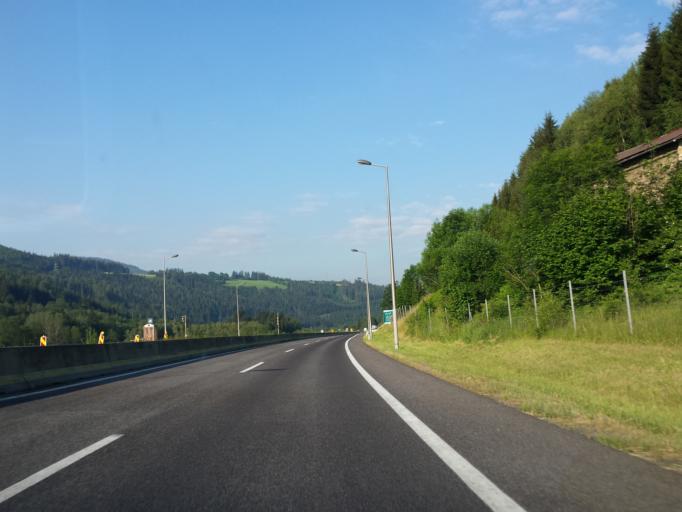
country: AT
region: Styria
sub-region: Politischer Bezirk Bruck-Muerzzuschlag
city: Spital am Semmering
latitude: 47.6100
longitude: 15.7395
